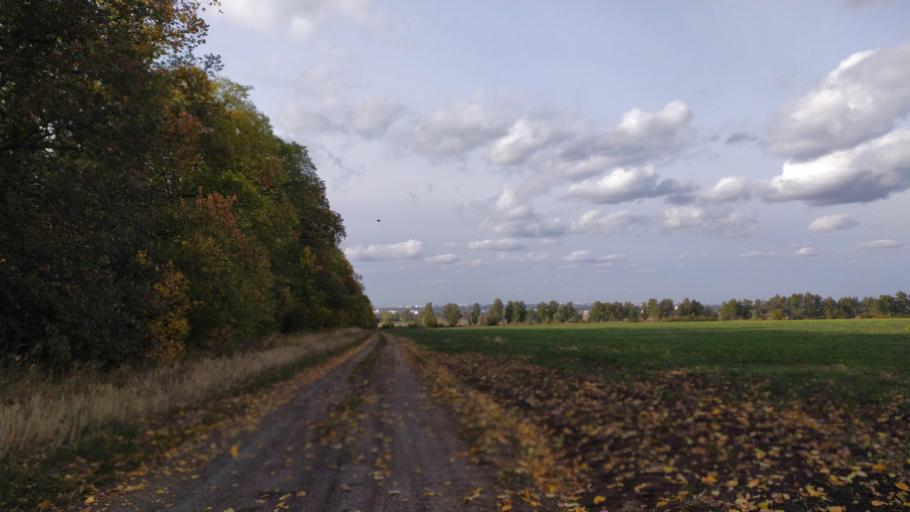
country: RU
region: Kursk
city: Kursk
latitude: 51.6175
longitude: 36.1638
